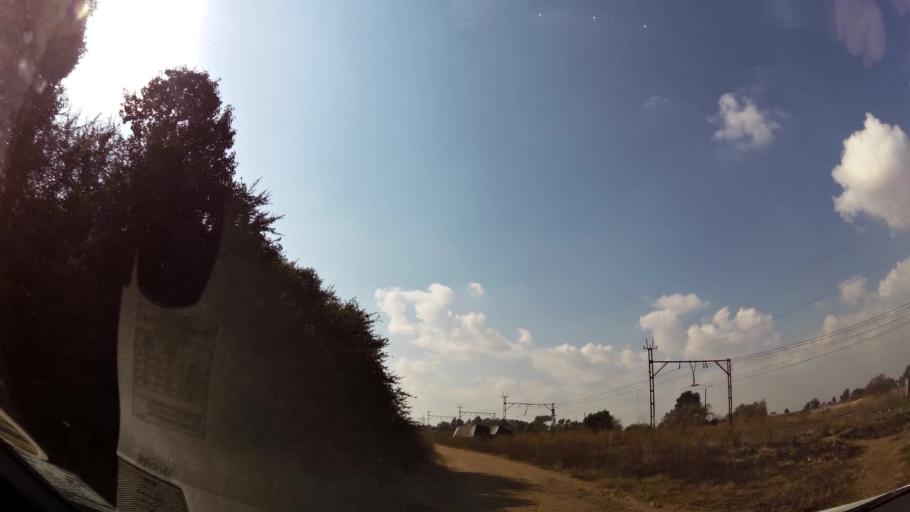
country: ZA
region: Gauteng
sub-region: Ekurhuleni Metropolitan Municipality
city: Springs
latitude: -26.1968
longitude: 28.5333
